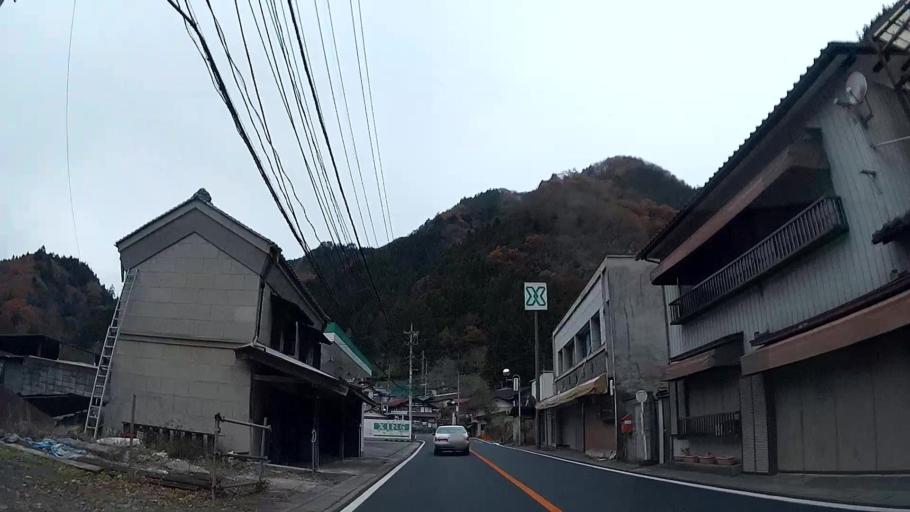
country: JP
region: Saitama
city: Chichibu
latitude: 35.9526
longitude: 138.9391
